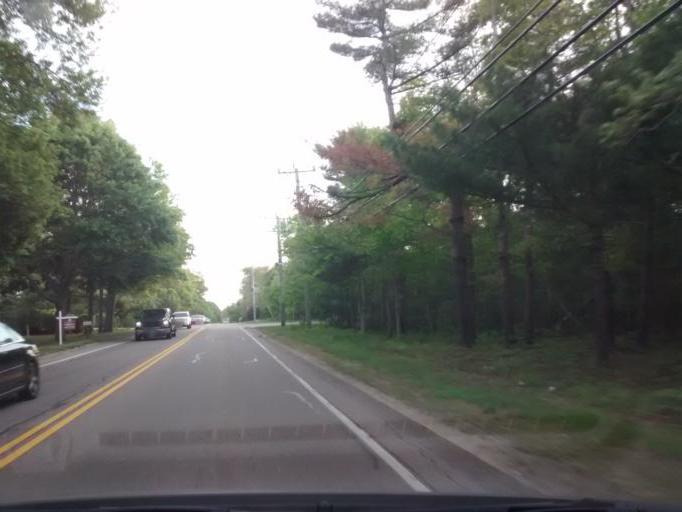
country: US
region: Massachusetts
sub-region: Barnstable County
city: Teaticket
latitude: 41.5849
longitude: -70.5869
